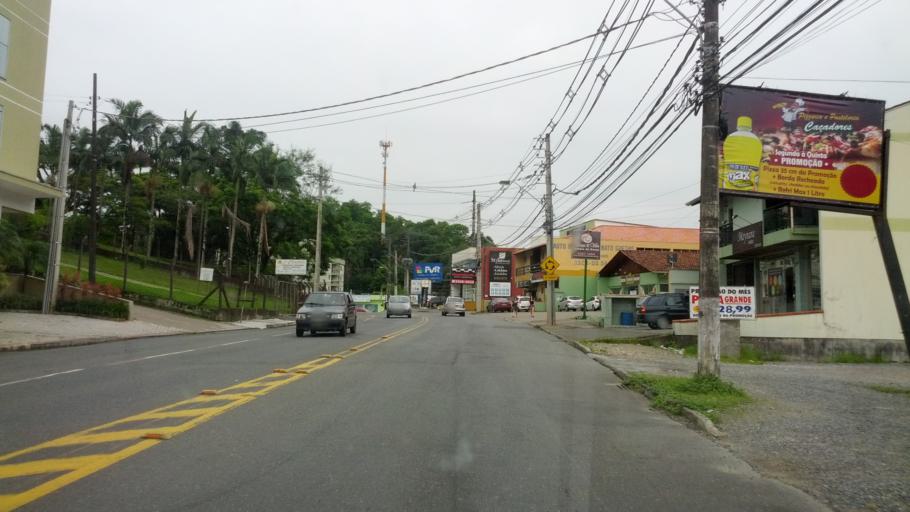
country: BR
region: Santa Catarina
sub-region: Blumenau
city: Blumenau
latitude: -26.9189
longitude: -49.1165
